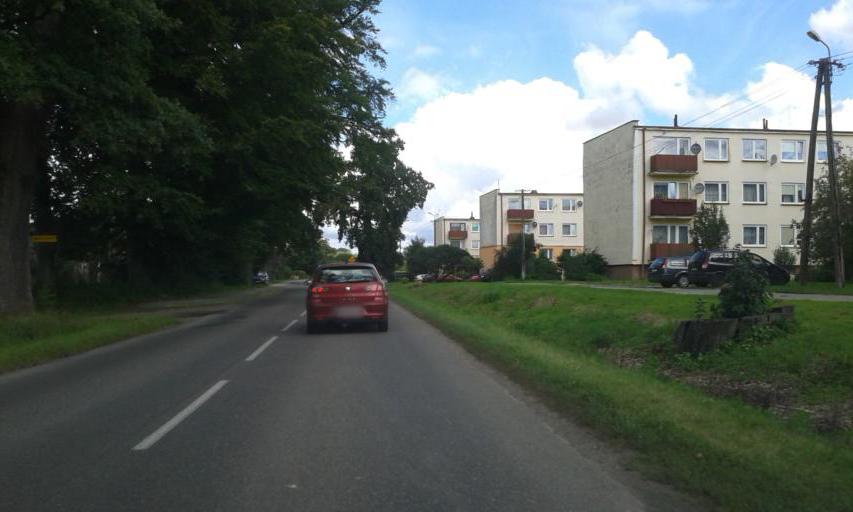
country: PL
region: West Pomeranian Voivodeship
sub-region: Powiat slawienski
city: Slawno
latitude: 54.2731
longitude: 16.6724
